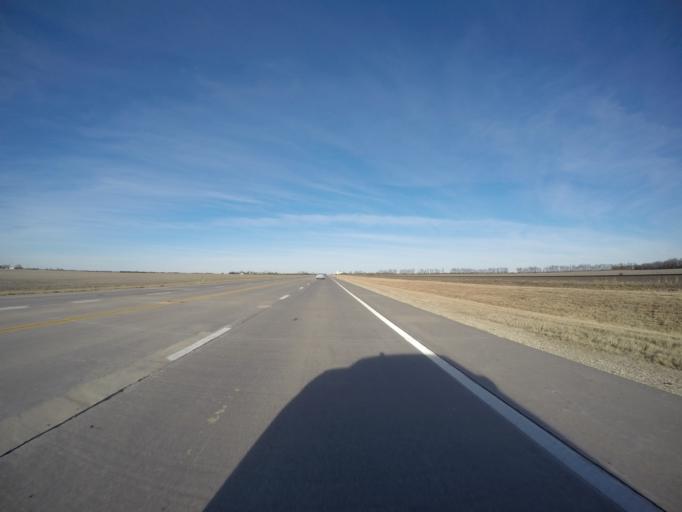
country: US
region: Kansas
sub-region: Harvey County
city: North Newton
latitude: 38.0958
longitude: -97.2814
